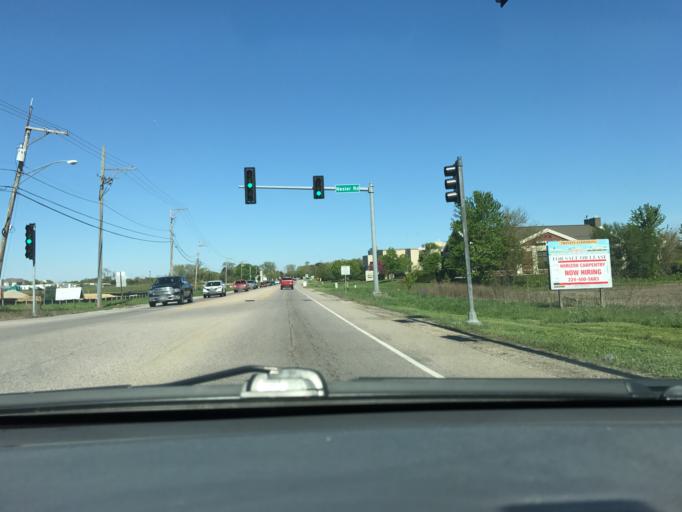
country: US
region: Illinois
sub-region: Kane County
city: Pingree Grove
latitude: 42.0394
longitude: -88.3634
